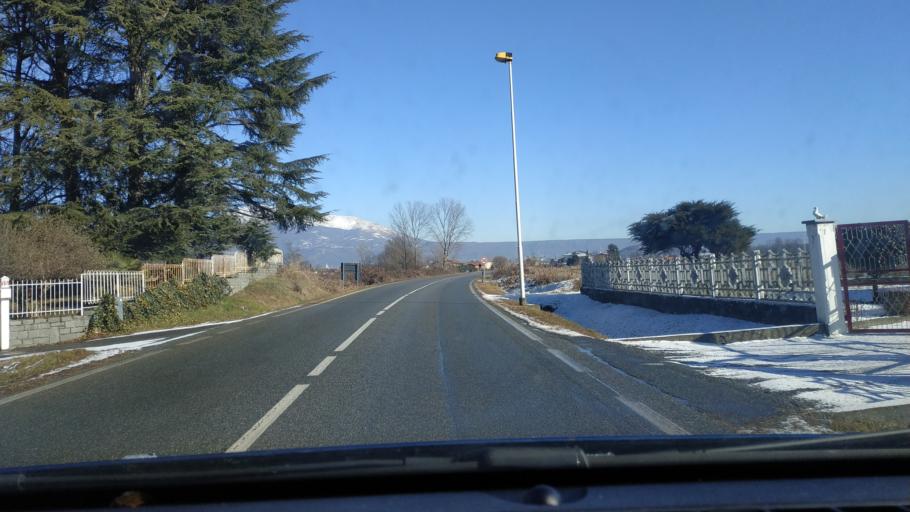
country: IT
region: Piedmont
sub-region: Provincia di Torino
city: Colleretto Giacosa
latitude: 45.4354
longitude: 7.8065
